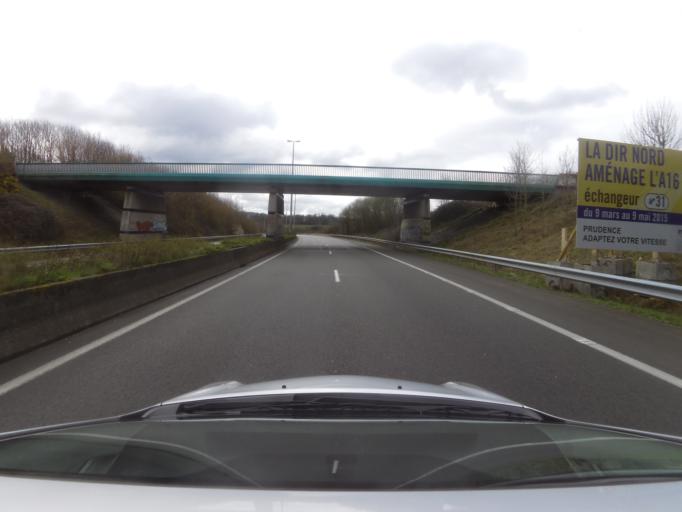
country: FR
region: Nord-Pas-de-Calais
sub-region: Departement du Pas-de-Calais
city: Saint-Martin-Boulogne
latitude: 50.7409
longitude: 1.6289
